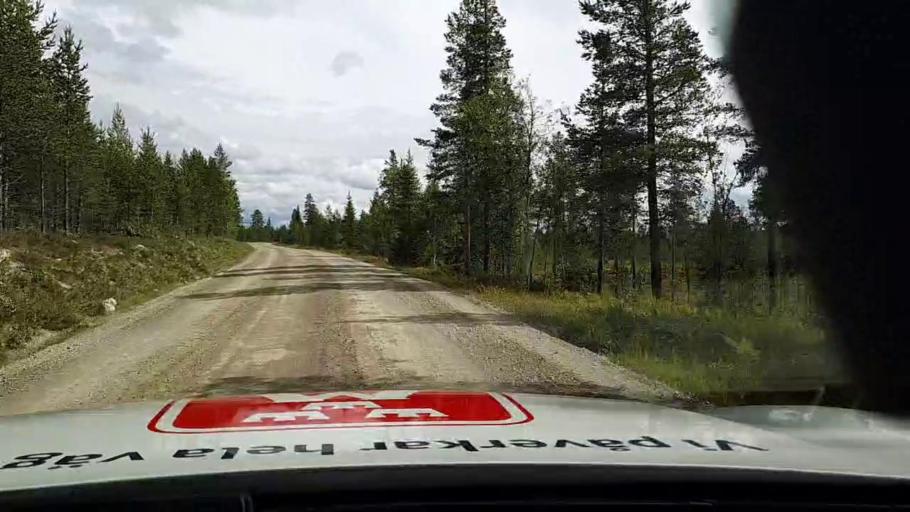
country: SE
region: Jaemtland
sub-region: Are Kommun
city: Jarpen
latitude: 62.5349
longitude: 13.4788
